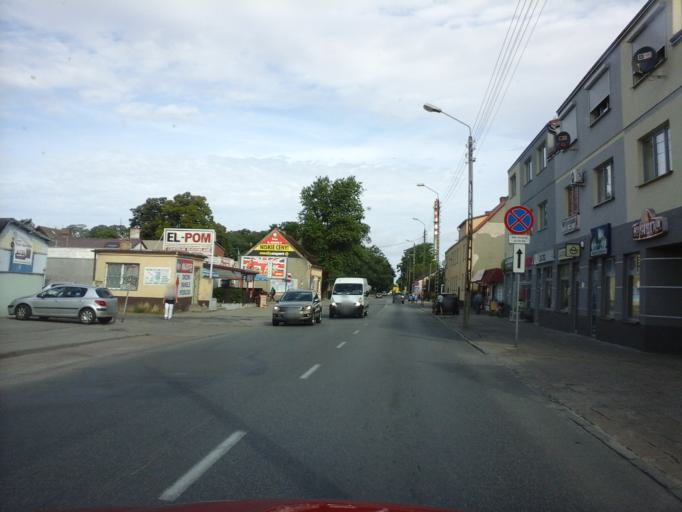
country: PL
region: West Pomeranian Voivodeship
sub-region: Powiat choszczenski
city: Choszczno
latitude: 53.1656
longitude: 15.4271
